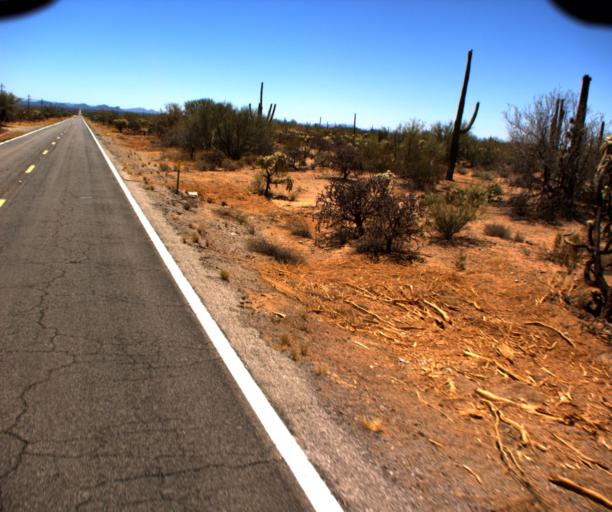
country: US
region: Arizona
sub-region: Pima County
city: Sells
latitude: 32.1153
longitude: -112.0778
